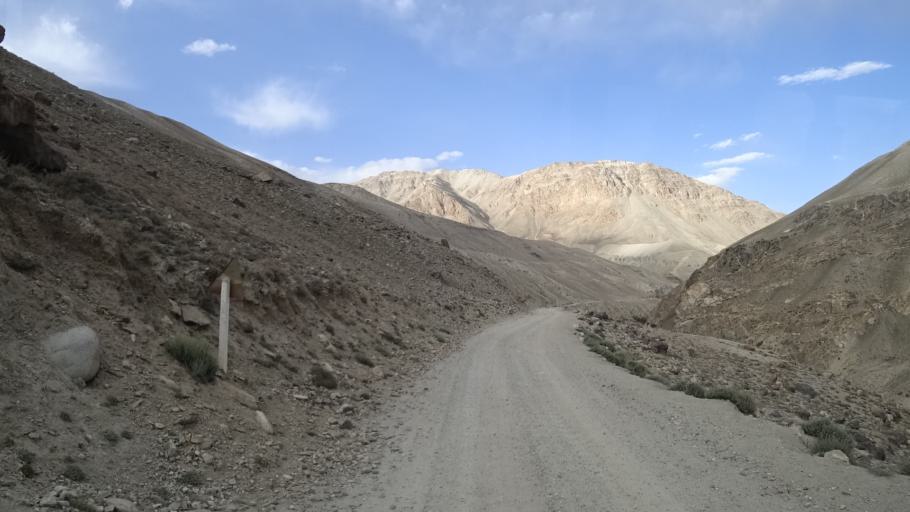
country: AF
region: Badakhshan
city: Khandud
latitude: 37.2289
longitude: 72.8093
